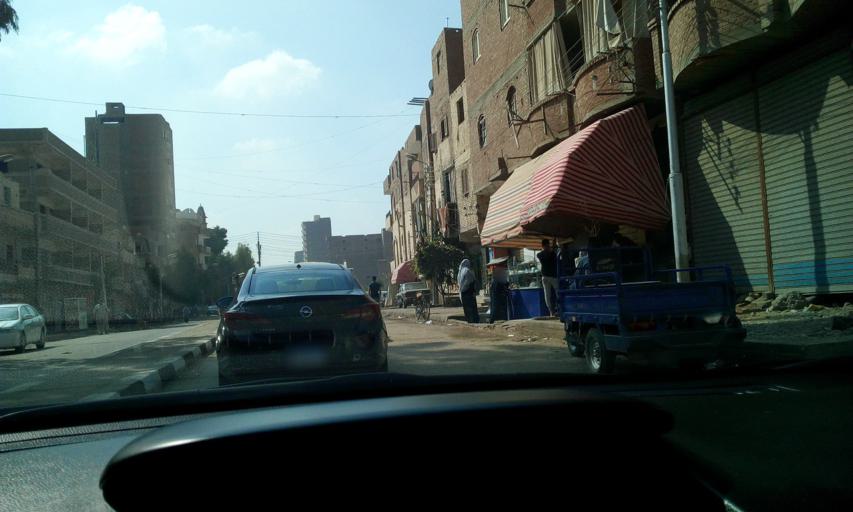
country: EG
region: Muhafazat al Fayyum
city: Al Fayyum
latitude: 29.3316
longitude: 30.8426
